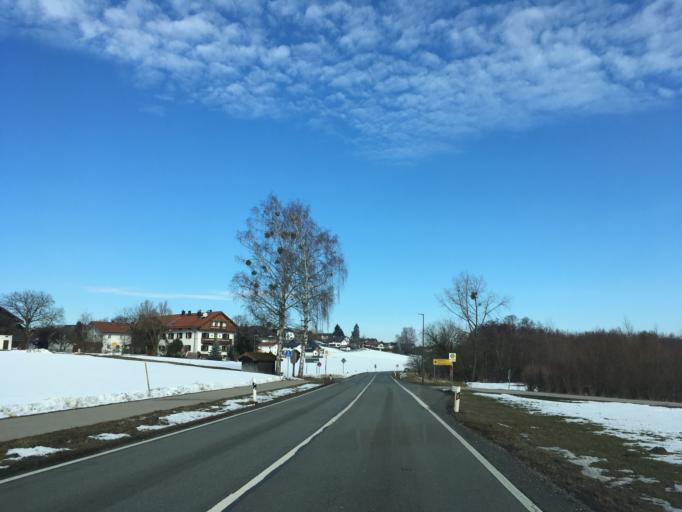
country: DE
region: Bavaria
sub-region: Upper Bavaria
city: Rosenheim
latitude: 47.8865
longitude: 12.1546
